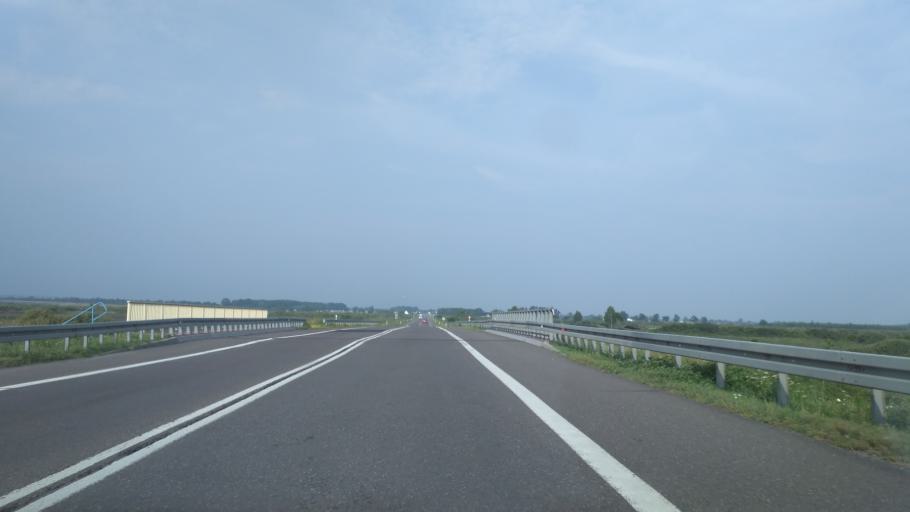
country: PL
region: Lublin Voivodeship
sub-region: Powiat swidnicki
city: Trawniki
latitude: 51.1650
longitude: 23.0507
